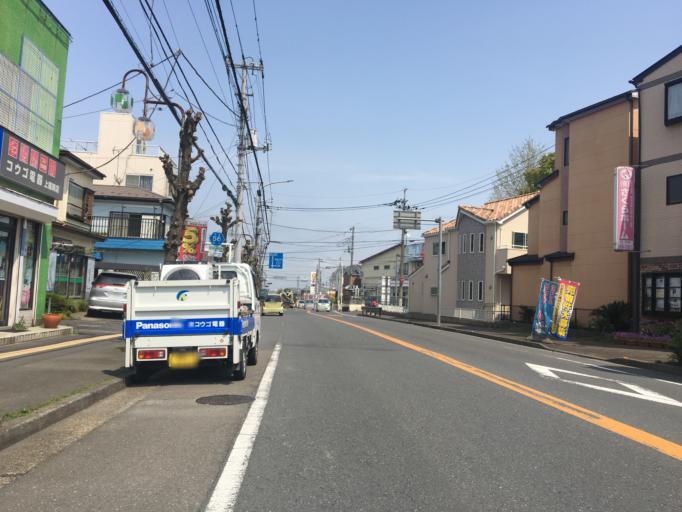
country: JP
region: Saitama
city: Kamifukuoka
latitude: 35.8844
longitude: 139.5218
